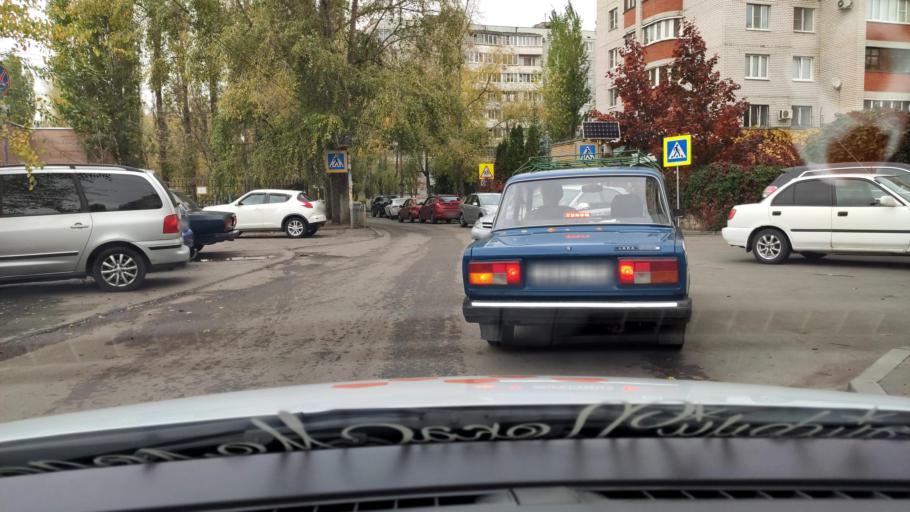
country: RU
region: Voronezj
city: Podgornoye
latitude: 51.7067
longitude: 39.1551
